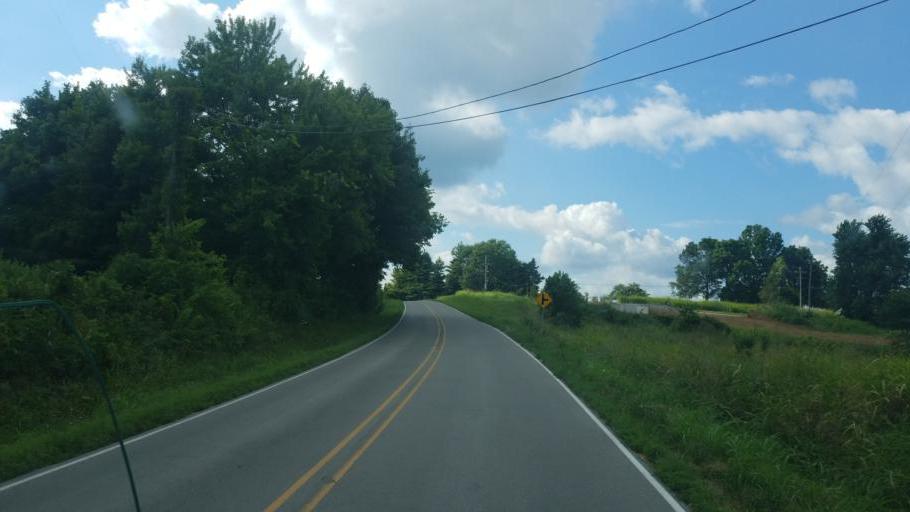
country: US
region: Illinois
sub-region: Union County
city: Cobden
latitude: 37.5548
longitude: -89.2965
